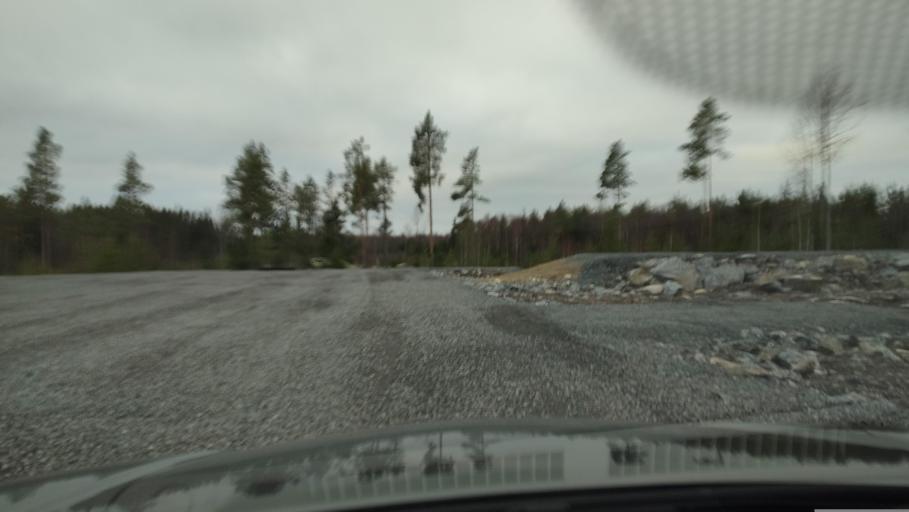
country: FI
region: Ostrobothnia
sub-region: Sydosterbotten
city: Kristinestad
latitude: 62.2008
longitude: 21.5469
